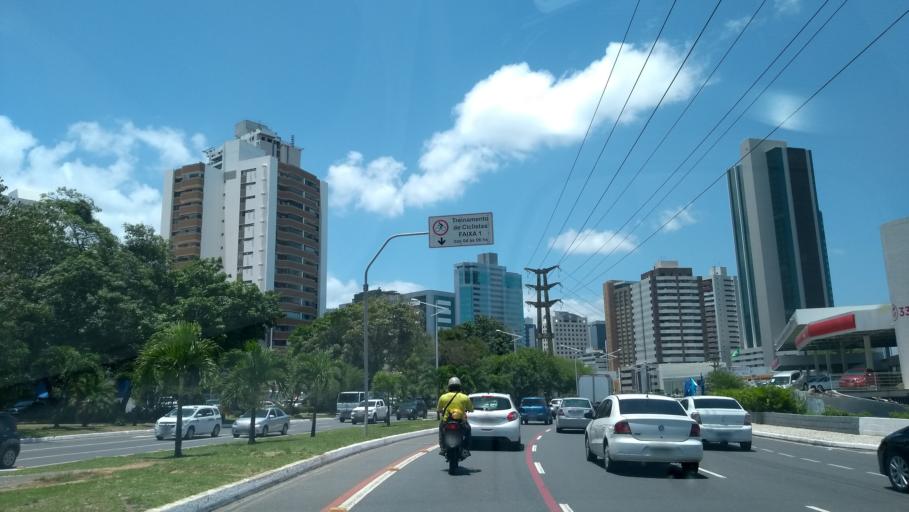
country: BR
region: Bahia
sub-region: Salvador
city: Salvador
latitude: -12.9906
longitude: -38.4500
